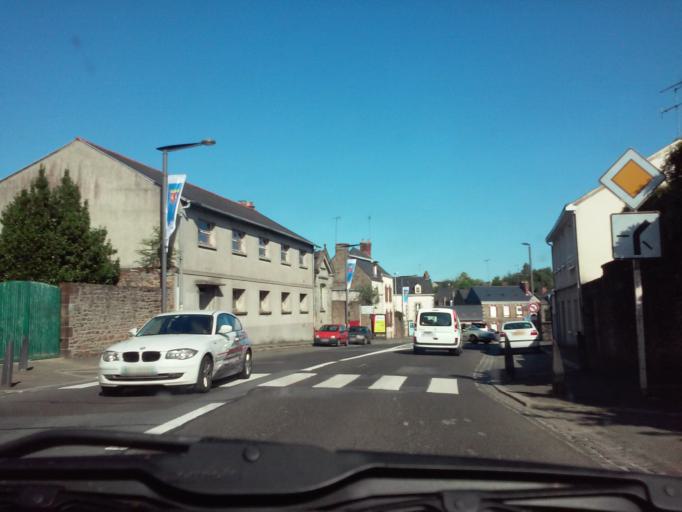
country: FR
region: Pays de la Loire
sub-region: Departement de la Mayenne
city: Ernee
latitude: 48.2962
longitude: -0.9330
